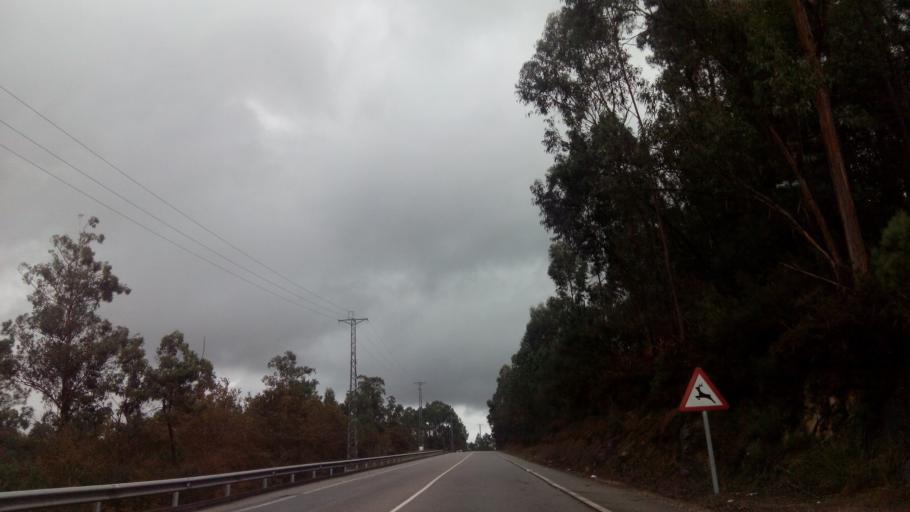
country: ES
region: Galicia
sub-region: Provincia de Pontevedra
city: Mondariz-Balneario
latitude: 42.2216
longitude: -8.4866
